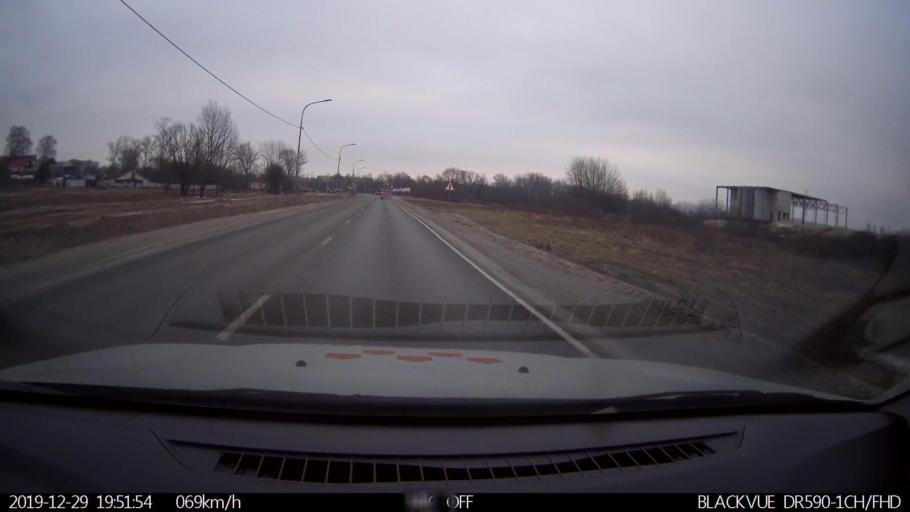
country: RU
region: Nizjnij Novgorod
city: Bor
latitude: 56.3574
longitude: 44.0482
